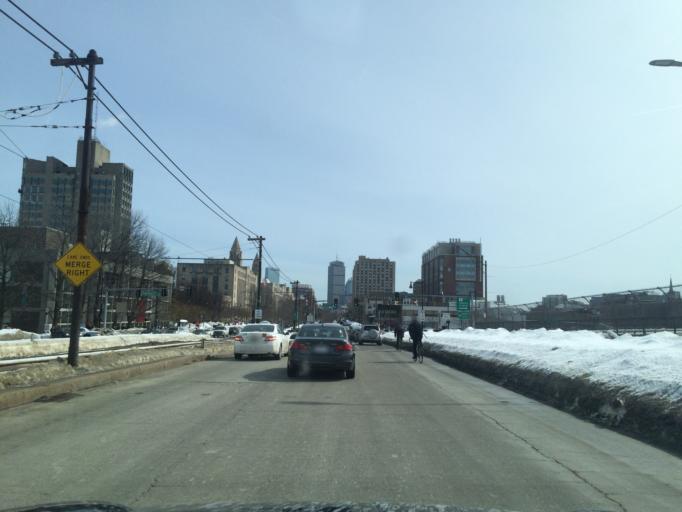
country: US
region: Massachusetts
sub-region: Norfolk County
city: Brookline
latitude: 42.3505
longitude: -71.1106
